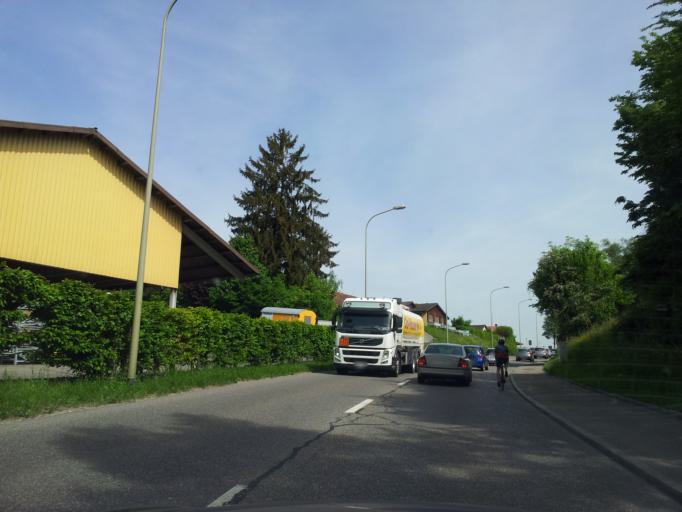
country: CH
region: Zurich
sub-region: Bezirk Buelach
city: Seglingen
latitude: 47.5789
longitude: 8.5159
